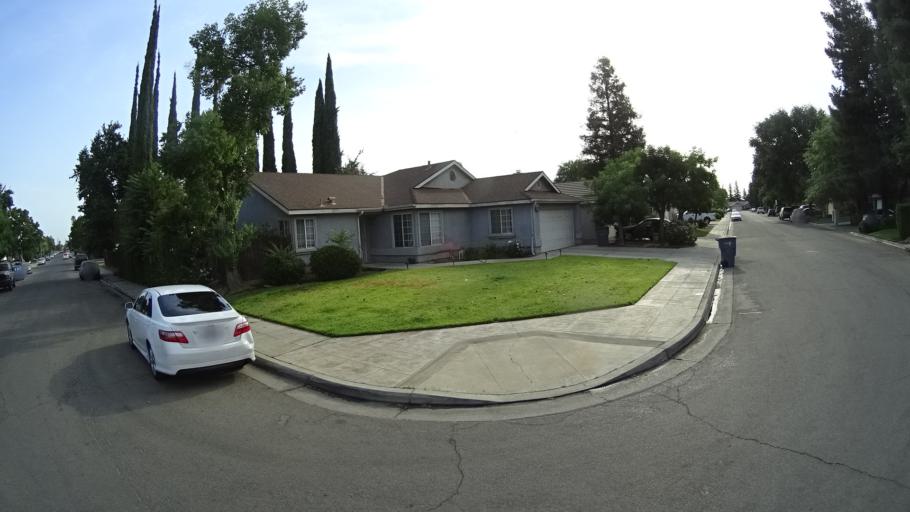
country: US
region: California
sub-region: Fresno County
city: West Park
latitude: 36.7739
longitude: -119.8664
